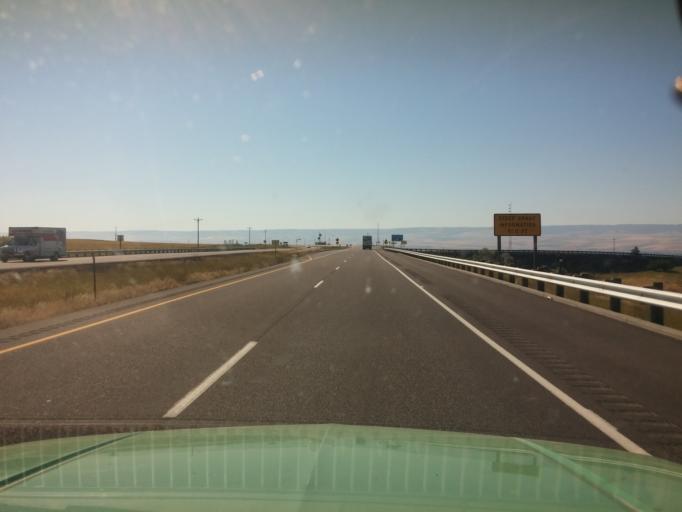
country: US
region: Idaho
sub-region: Nez Perce County
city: Lewiston
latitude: 46.4644
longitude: -117.0222
